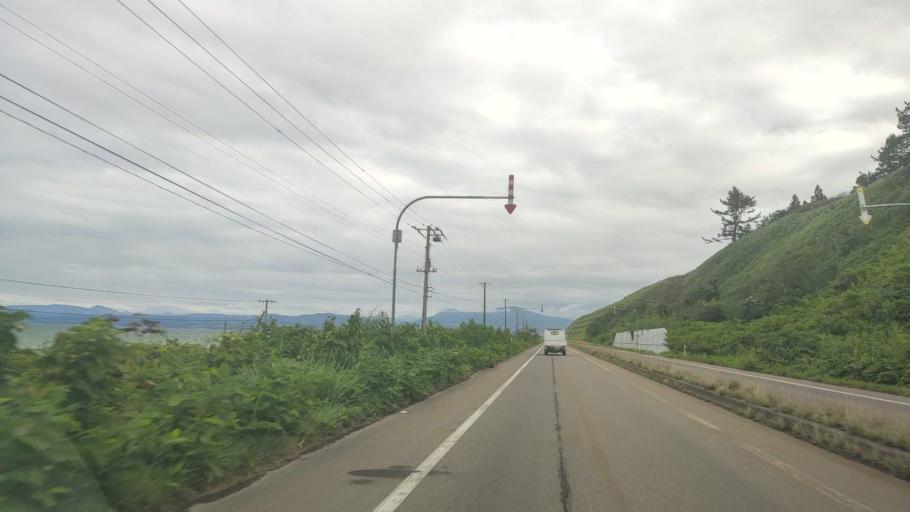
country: JP
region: Hokkaido
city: Niseko Town
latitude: 42.3317
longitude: 140.2781
